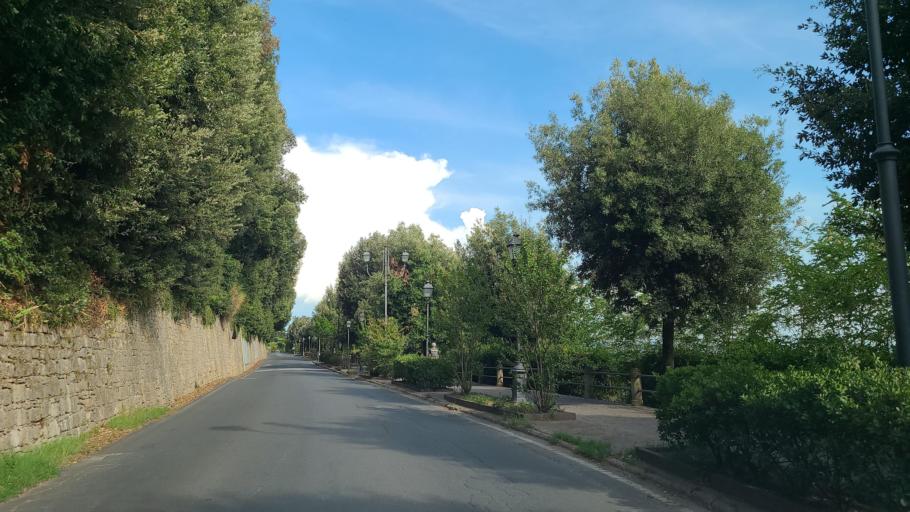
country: IT
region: Tuscany
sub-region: Province of Pisa
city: Volterra
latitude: 43.4000
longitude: 10.8604
